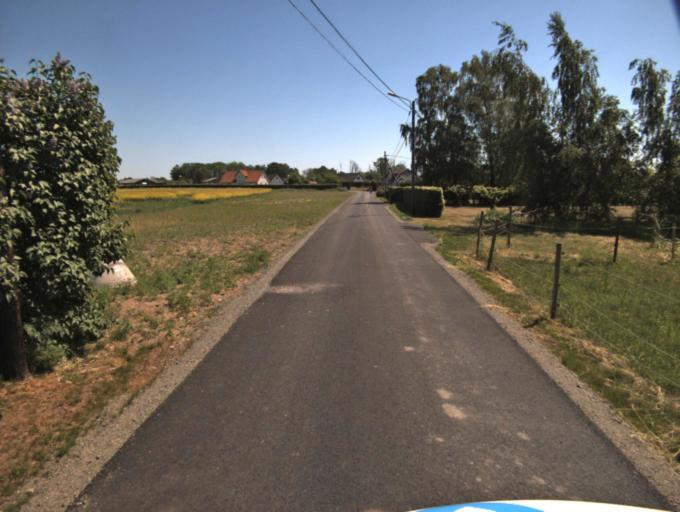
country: SE
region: Skane
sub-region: Kristianstads Kommun
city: Kristianstad
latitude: 56.0146
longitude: 14.2152
